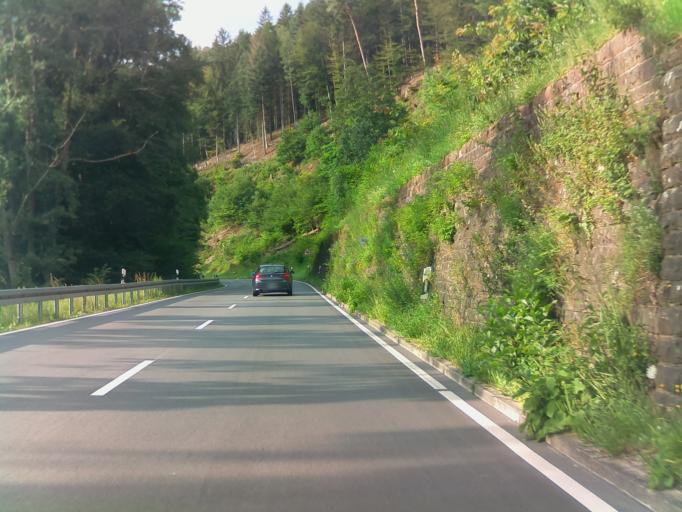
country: DE
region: Baden-Wuerttemberg
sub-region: Karlsruhe Region
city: Schonau
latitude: 49.4480
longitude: 8.8106
